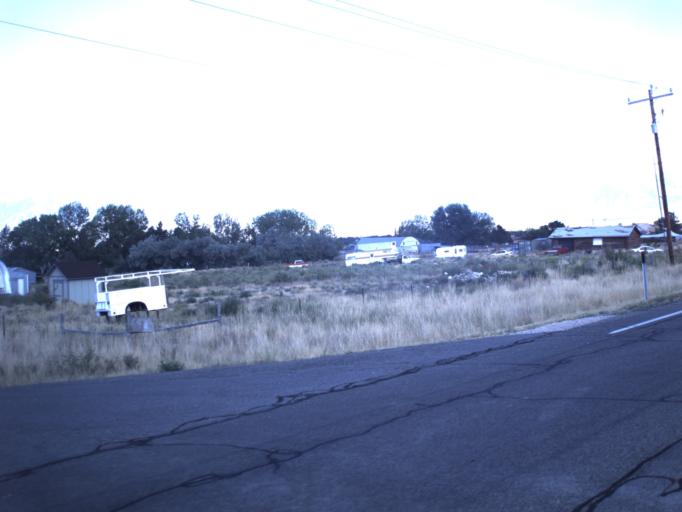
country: US
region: Utah
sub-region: Tooele County
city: Grantsville
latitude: 40.6129
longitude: -112.4954
